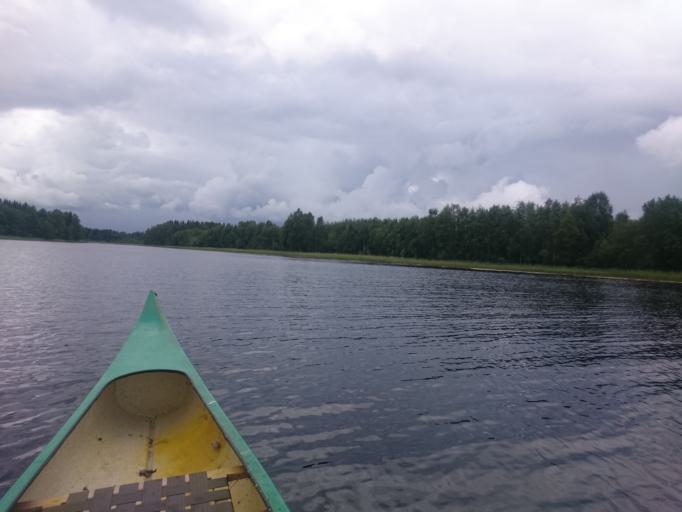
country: SE
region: Vaesternorrland
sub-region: OErnskoeldsviks Kommun
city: Ornskoldsvik
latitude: 63.6477
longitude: 18.6179
